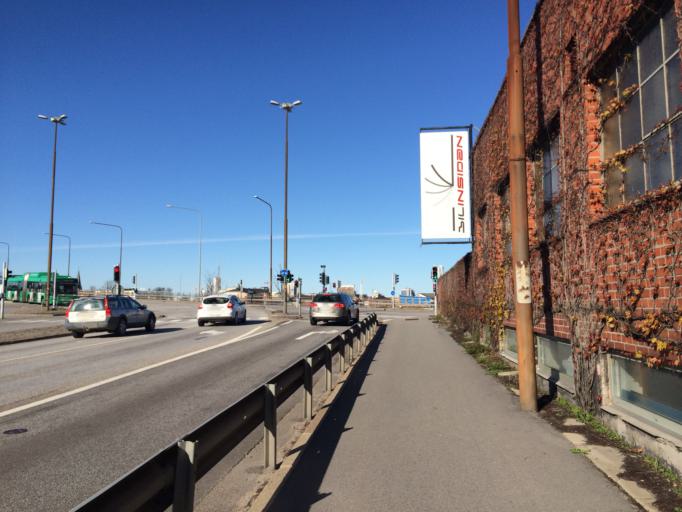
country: SE
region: Skane
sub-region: Malmo
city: Malmoe
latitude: 55.6151
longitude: 13.0214
